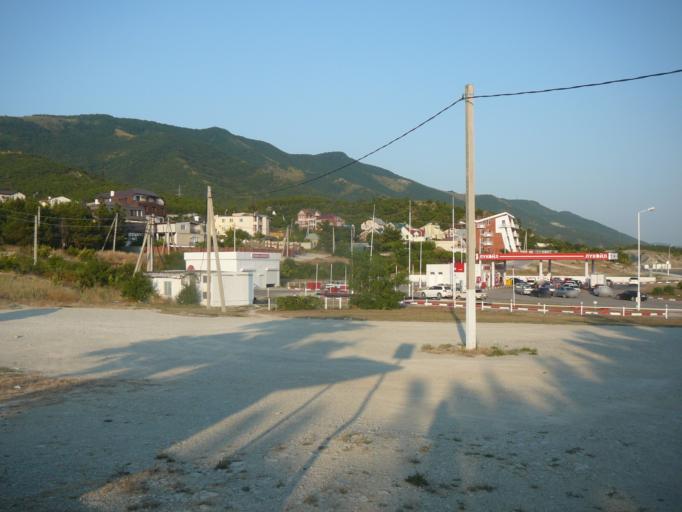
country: RU
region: Krasnodarskiy
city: Gelendzhik
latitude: 44.5968
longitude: 38.0438
